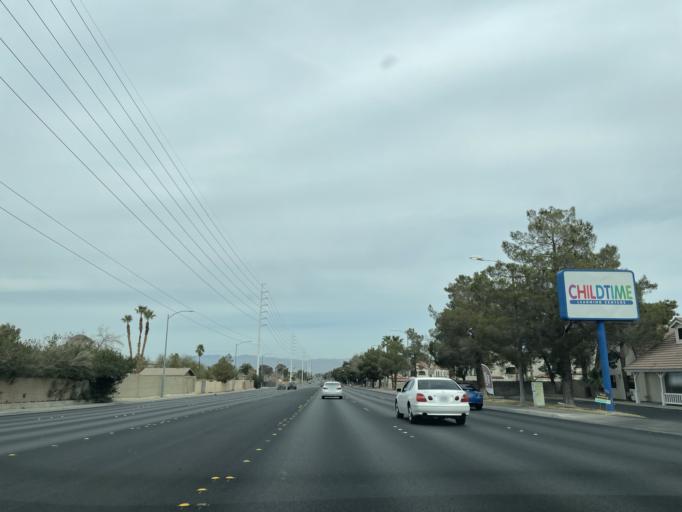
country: US
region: Nevada
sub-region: Clark County
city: Whitney
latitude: 36.0439
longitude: -115.1182
